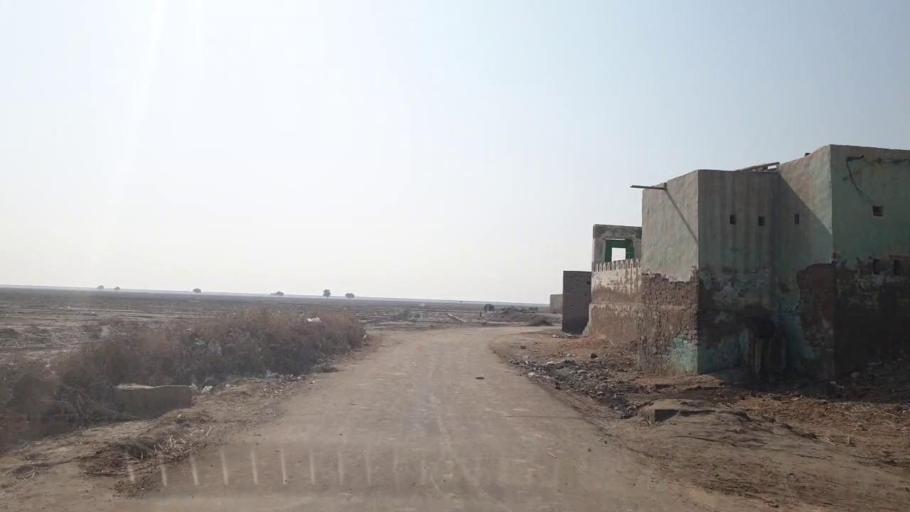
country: PK
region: Sindh
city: Bhan
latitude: 26.4352
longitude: 67.7352
